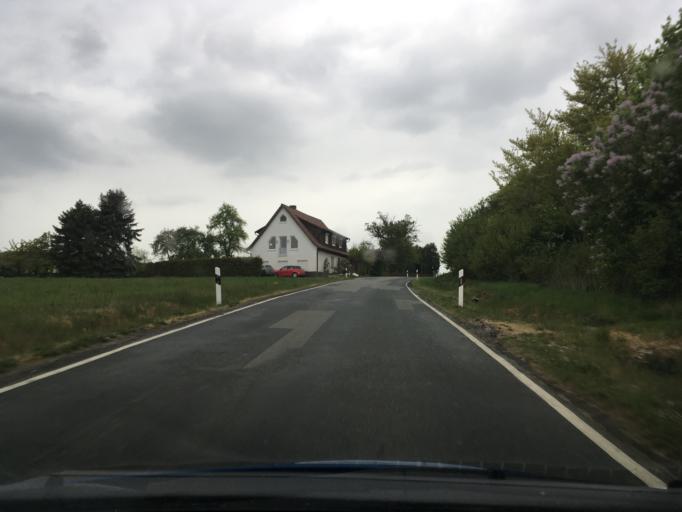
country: DE
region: Lower Saxony
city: Einbeck
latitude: 51.8387
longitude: 9.8232
